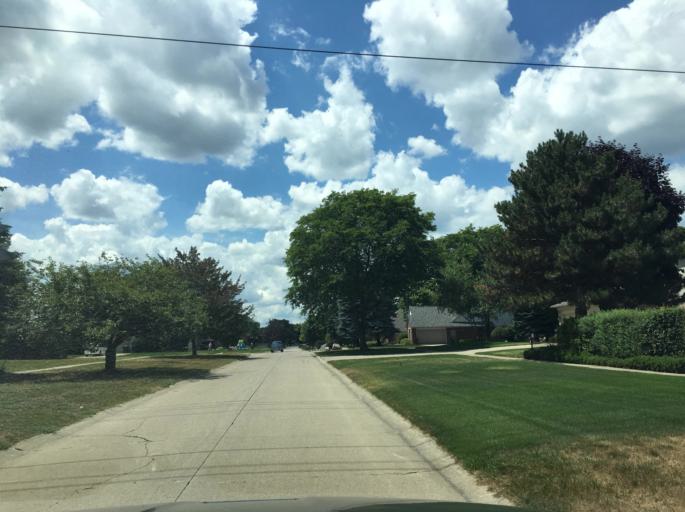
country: US
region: Michigan
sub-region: Macomb County
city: Utica
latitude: 42.6343
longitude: -83.0029
